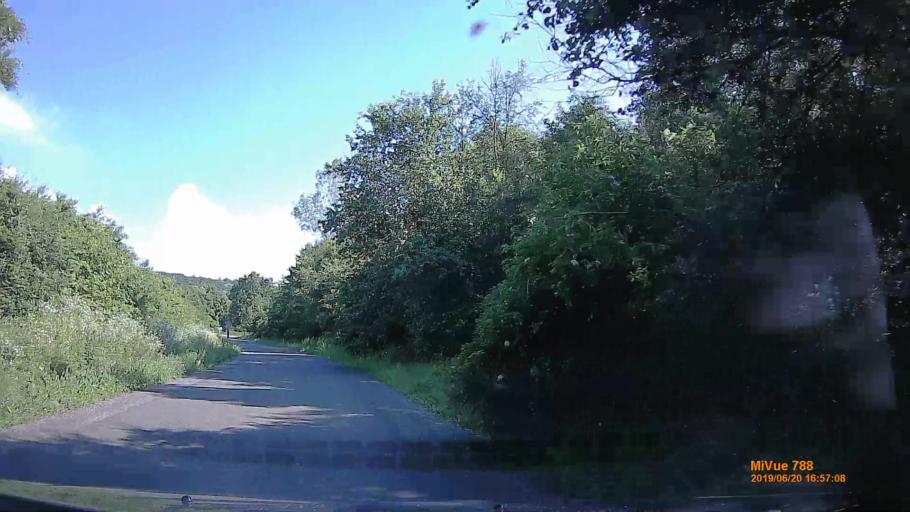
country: HU
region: Baranya
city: Buekkoesd
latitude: 46.1451
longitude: 18.0597
